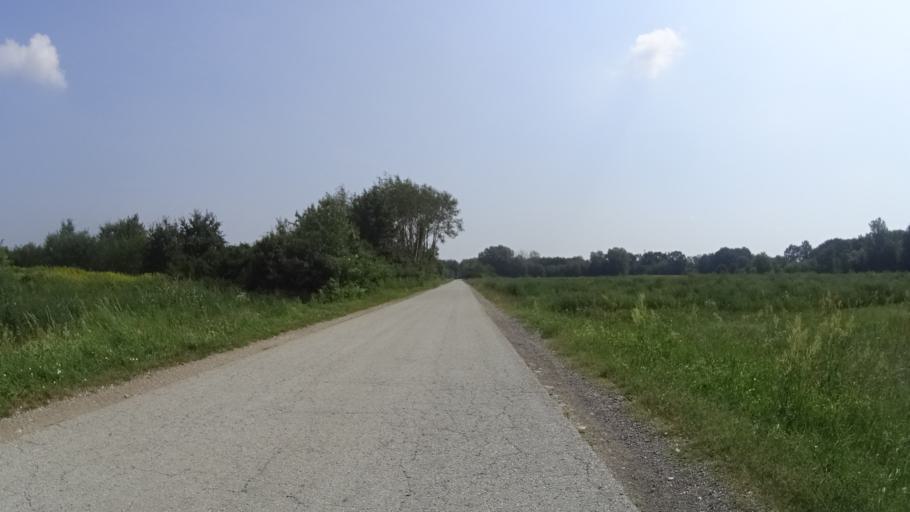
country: HR
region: Medimurska
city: Hodosan
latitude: 46.3950
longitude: 16.6169
